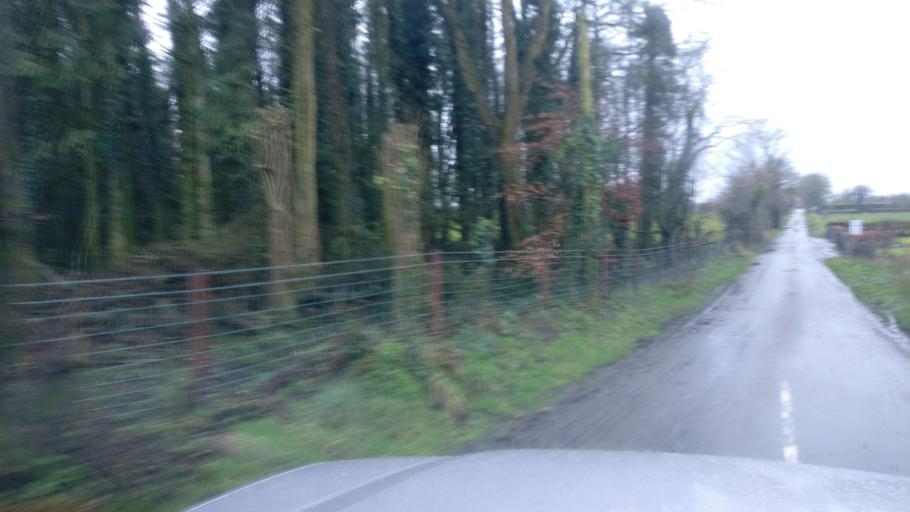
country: IE
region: Connaught
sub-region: County Galway
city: Ballinasloe
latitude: 53.2766
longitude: -8.3068
